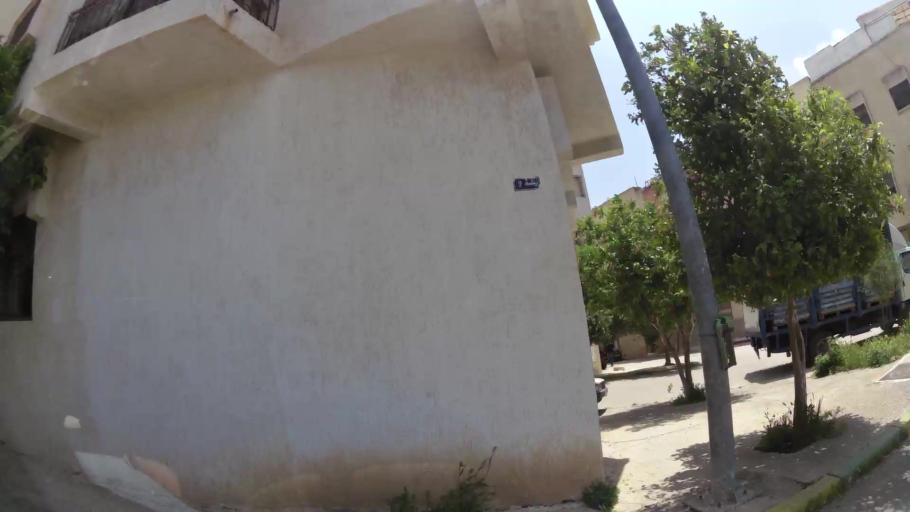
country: MA
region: Fes-Boulemane
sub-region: Fes
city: Fes
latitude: 34.0587
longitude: -5.0414
